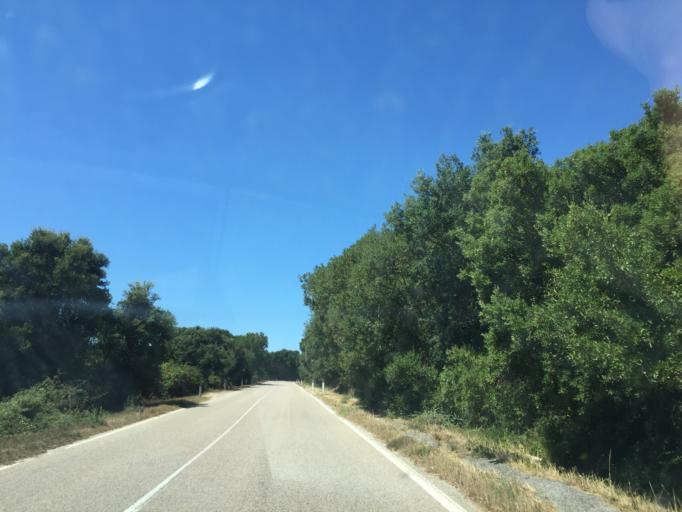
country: IT
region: Sardinia
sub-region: Provincia di Olbia-Tempio
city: Aggius
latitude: 40.9848
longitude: 9.0849
